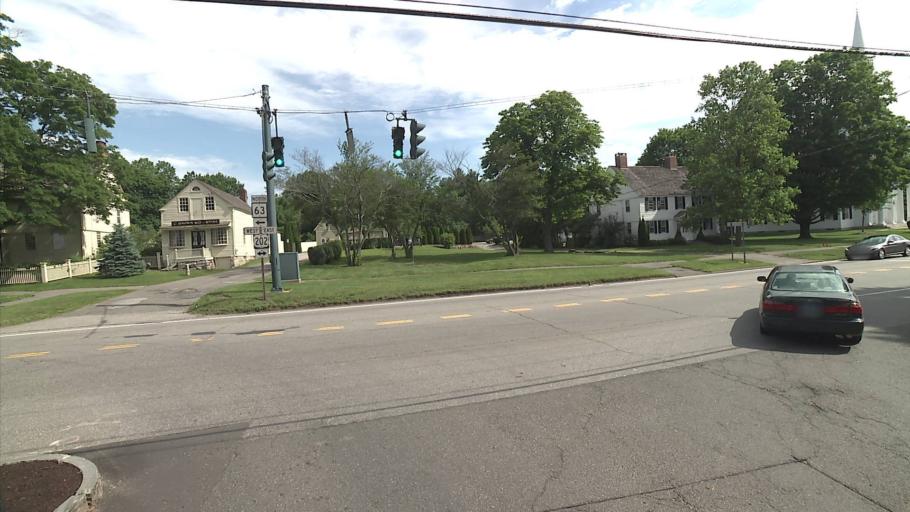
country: US
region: Connecticut
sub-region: Litchfield County
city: Litchfield
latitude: 41.7474
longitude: -73.1892
